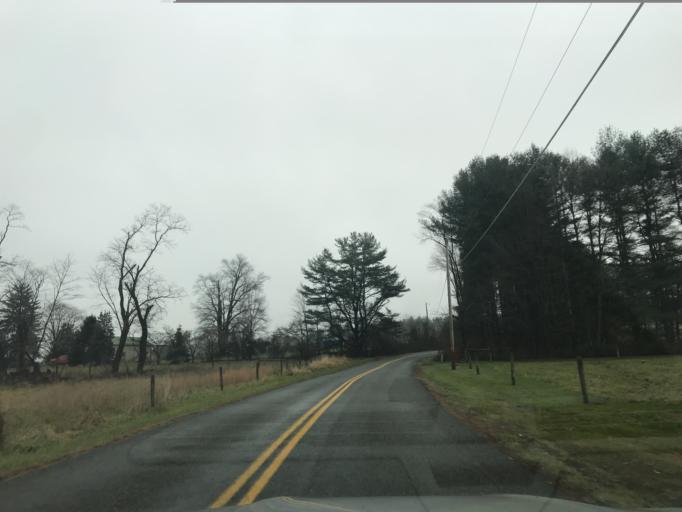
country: US
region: Maryland
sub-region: Harford County
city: South Bel Air
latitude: 39.5932
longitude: -76.2855
